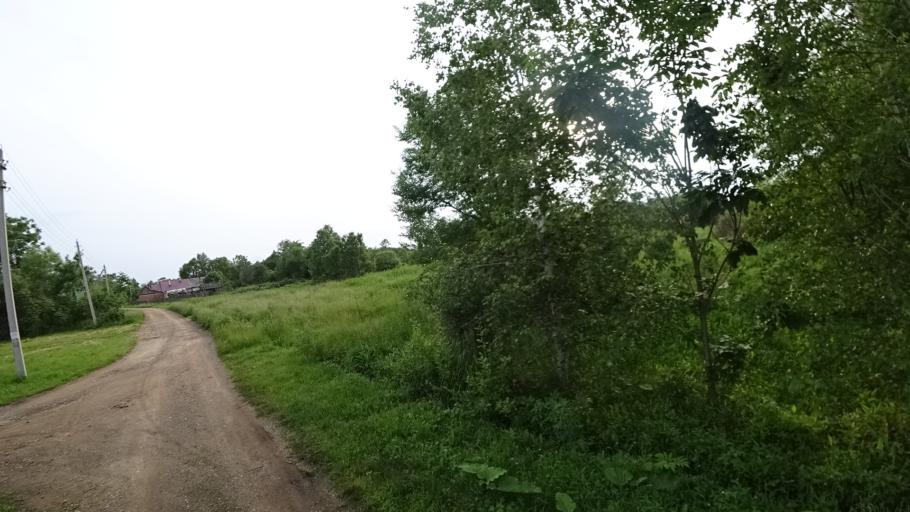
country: RU
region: Primorskiy
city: Novosysoyevka
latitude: 44.2454
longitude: 133.3615
